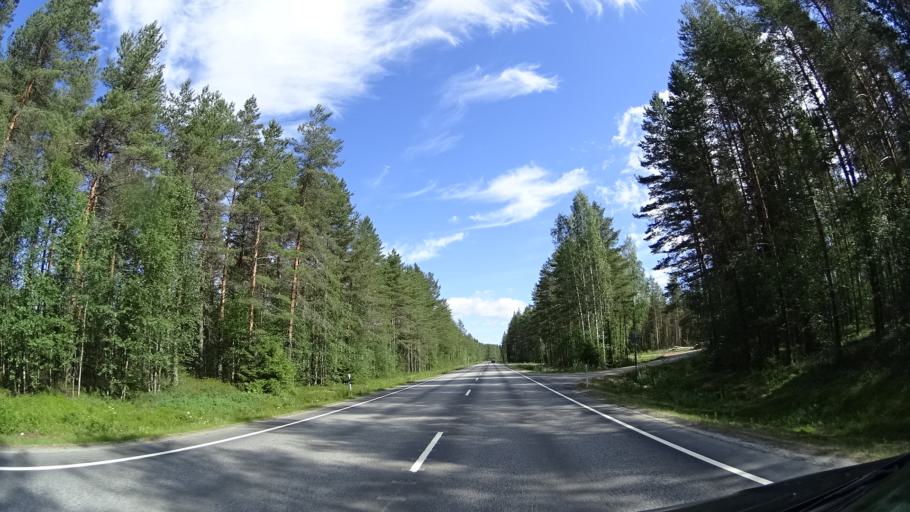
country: FI
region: Pirkanmaa
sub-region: Luoteis-Pirkanmaa
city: Kihnioe
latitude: 62.1182
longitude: 23.1061
